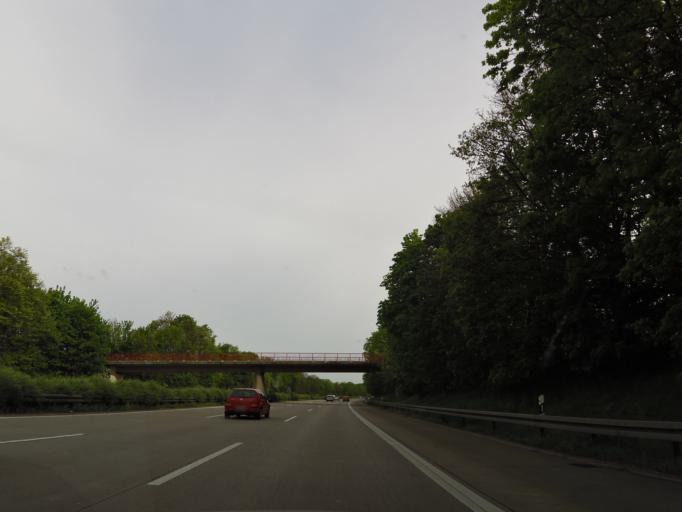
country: DE
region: Lower Saxony
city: Harsum
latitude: 52.2046
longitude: 9.9371
